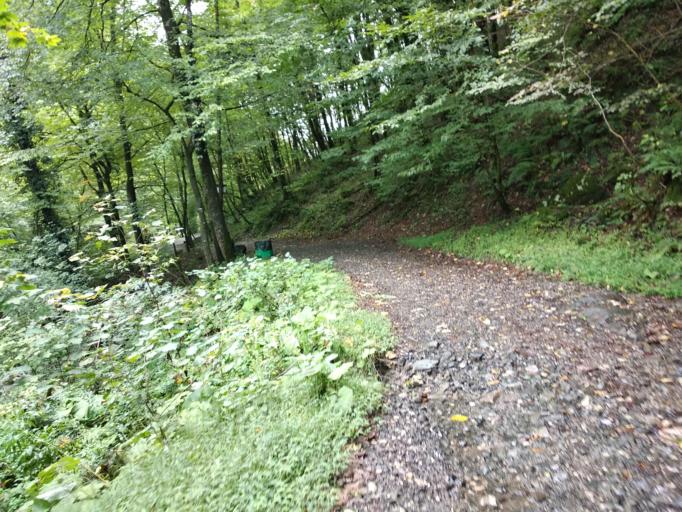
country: RU
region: Krasnodarskiy
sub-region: Sochi City
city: Sochi
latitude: 43.6383
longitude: 39.8113
